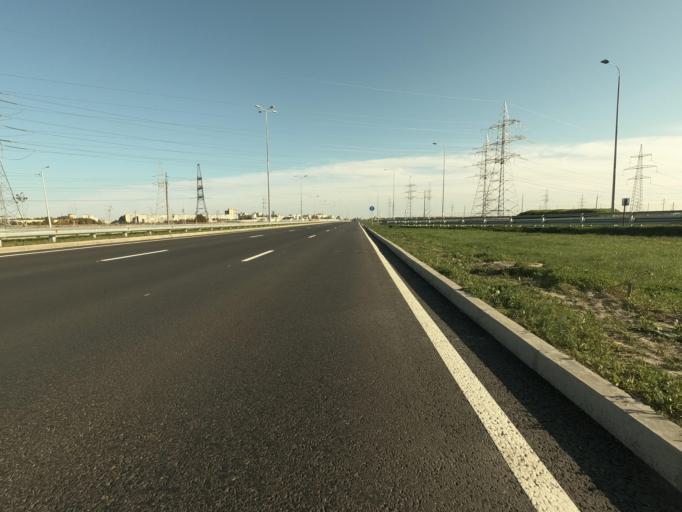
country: RU
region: St.-Petersburg
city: Kolpino
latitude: 59.7427
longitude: 30.5426
